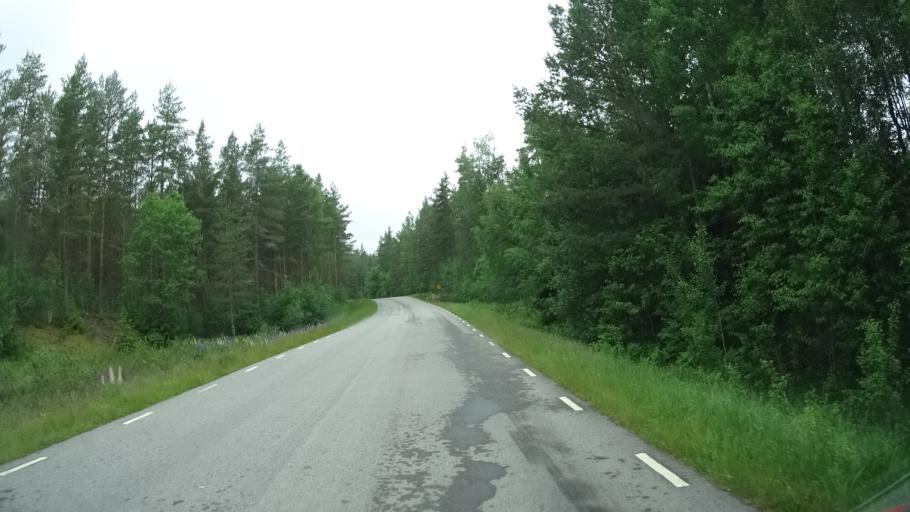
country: SE
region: Joenkoeping
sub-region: Eksjo Kommun
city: Mariannelund
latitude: 57.6863
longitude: 15.6815
